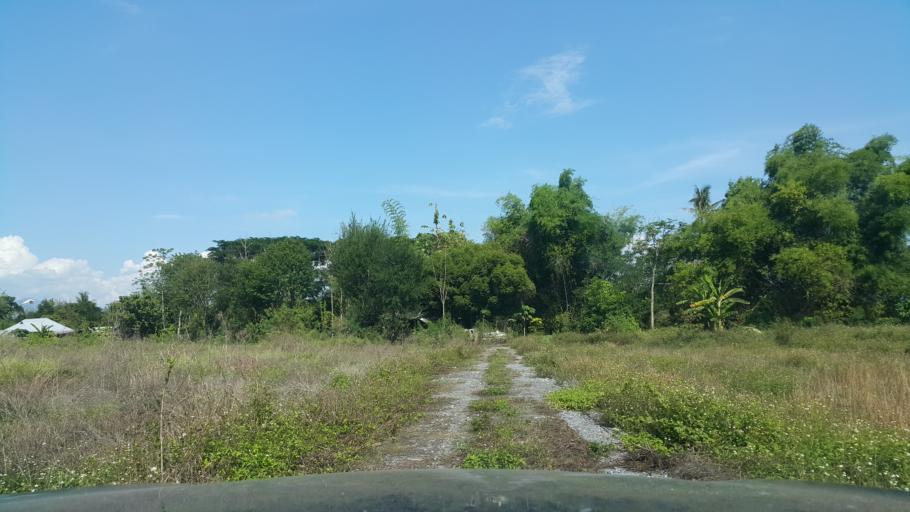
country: TH
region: Chiang Mai
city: San Kamphaeng
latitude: 18.8043
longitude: 99.1213
